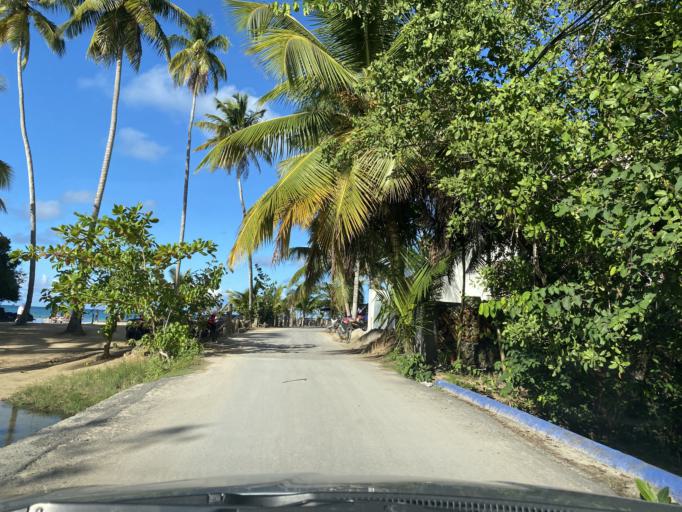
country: DO
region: Samana
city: Las Terrenas
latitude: 19.3183
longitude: -69.5572
